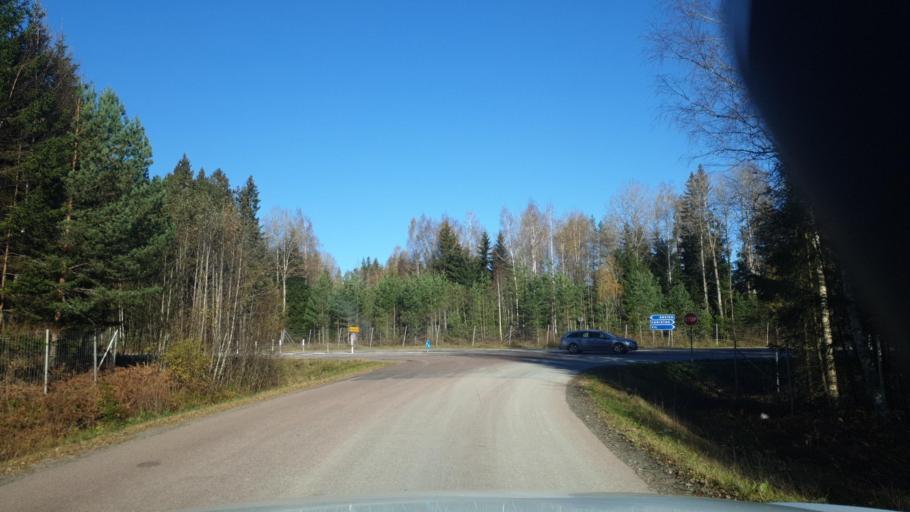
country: SE
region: Vaermland
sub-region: Karlstads Kommun
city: Edsvalla
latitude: 59.5114
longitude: 13.2074
